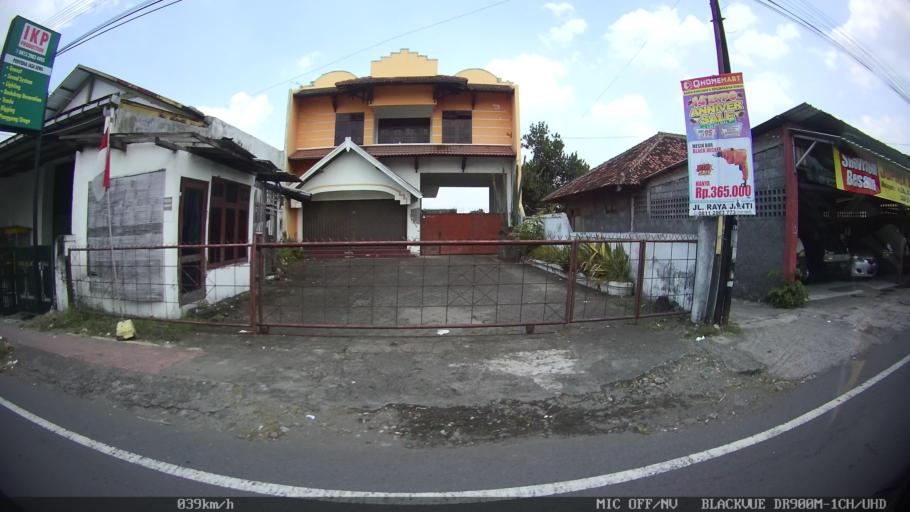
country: ID
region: Daerah Istimewa Yogyakarta
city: Yogyakarta
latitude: -7.8109
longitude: 110.4045
